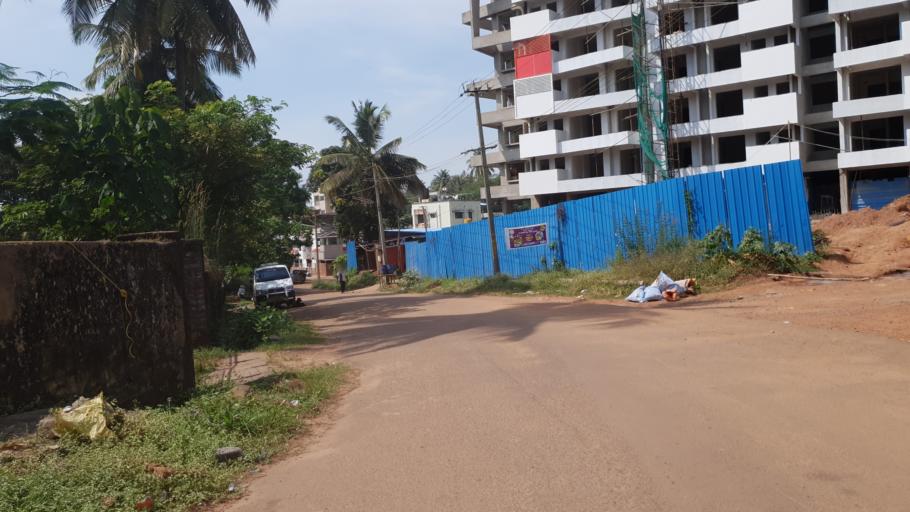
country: IN
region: Karnataka
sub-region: Dakshina Kannada
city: Ullal
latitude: 12.8441
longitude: 74.8450
